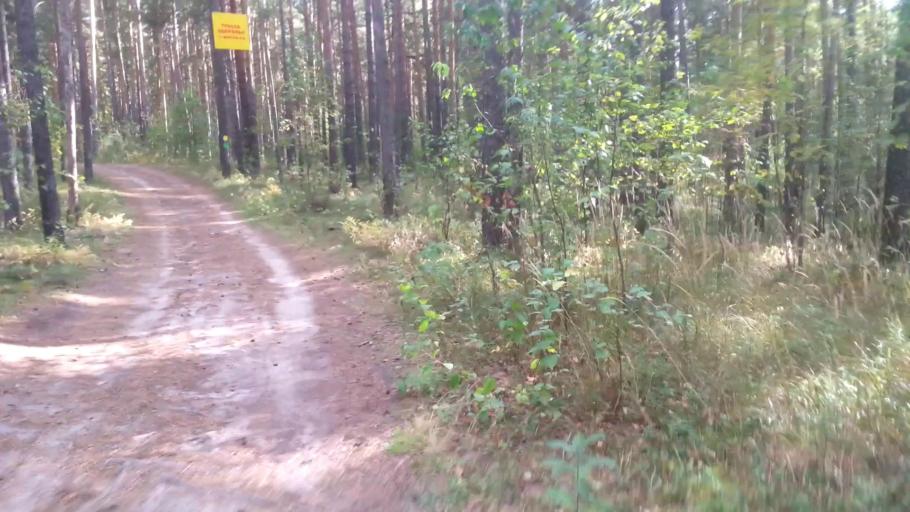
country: RU
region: Altai Krai
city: Yuzhnyy
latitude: 53.2844
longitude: 83.6990
